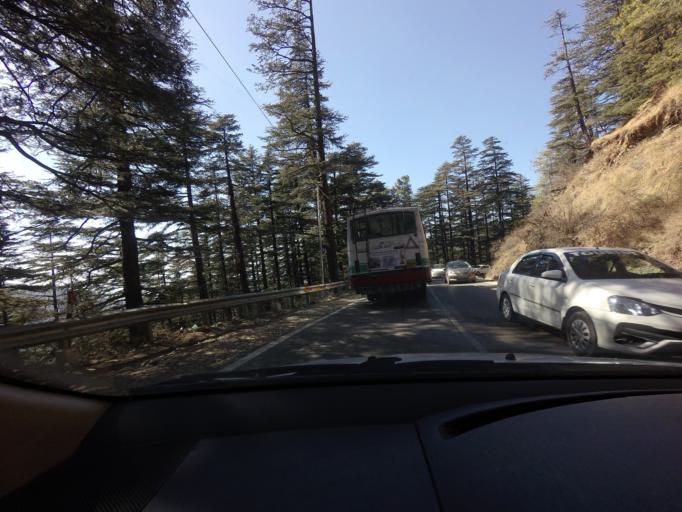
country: IN
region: Himachal Pradesh
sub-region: Shimla
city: Shimla
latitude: 31.1188
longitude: 77.2353
